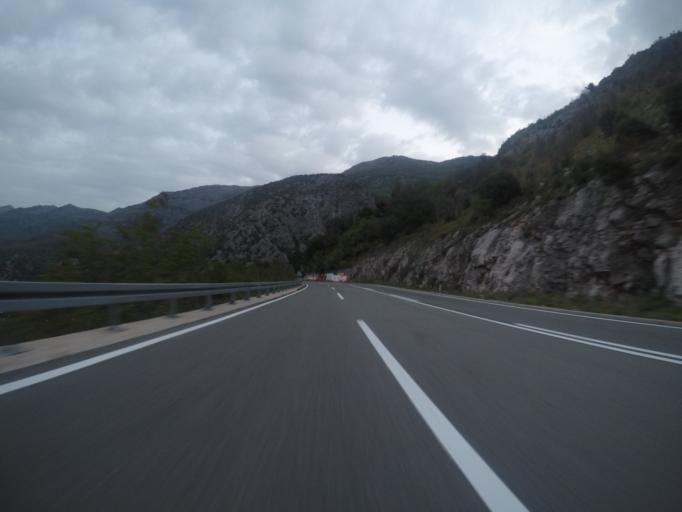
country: ME
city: Petrovac na Moru
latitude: 42.1872
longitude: 18.9886
